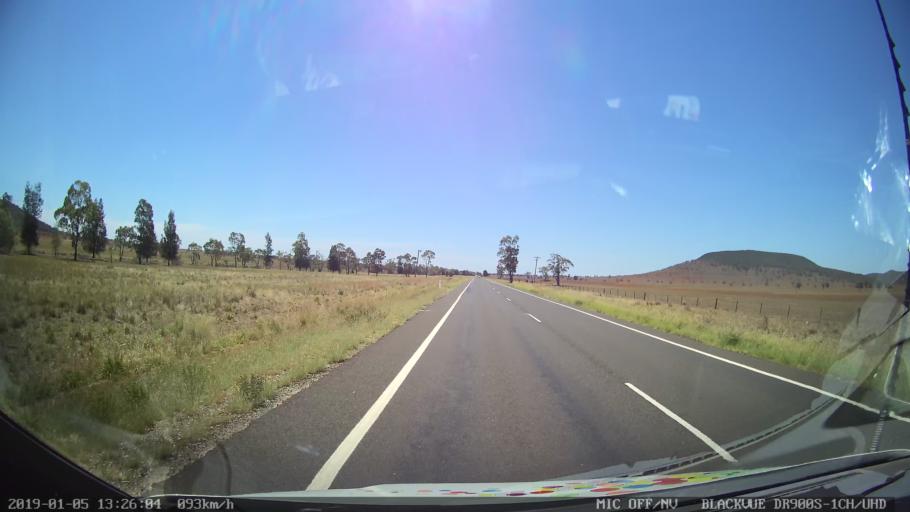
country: AU
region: New South Wales
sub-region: Gunnedah
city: Gunnedah
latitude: -31.0561
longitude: 150.0106
